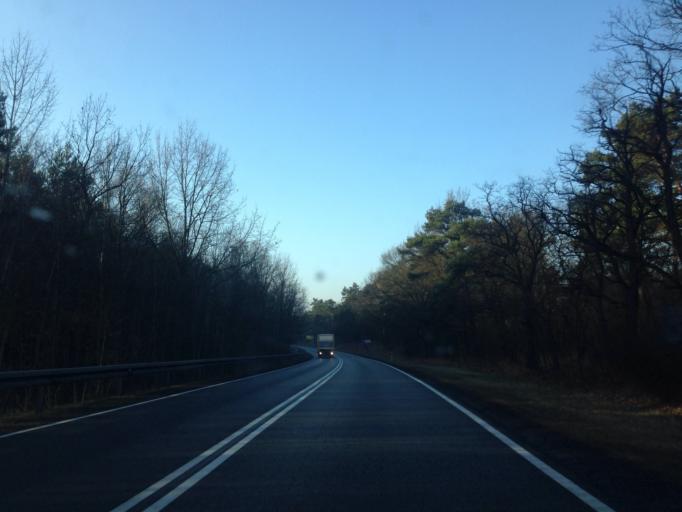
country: PL
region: Kujawsko-Pomorskie
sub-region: Powiat torunski
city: Zlawies Wielka
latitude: 53.0497
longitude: 18.3576
